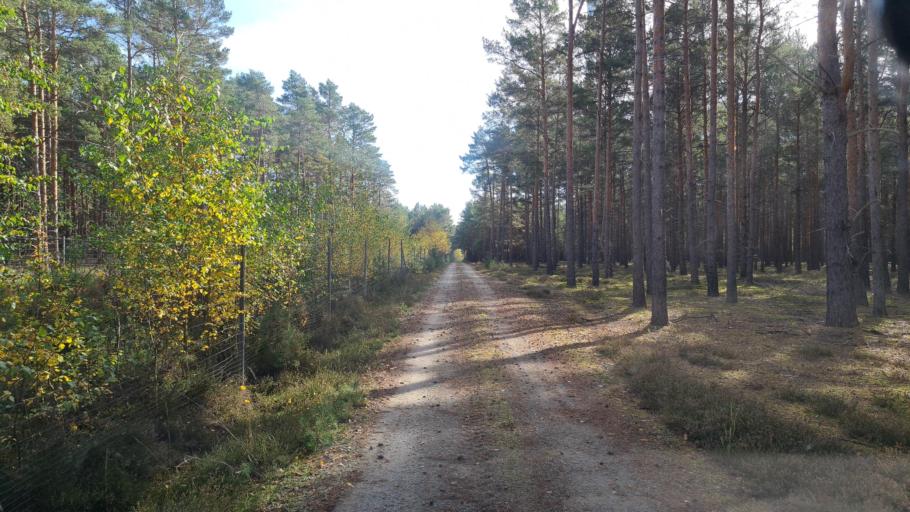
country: DE
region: Brandenburg
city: Sallgast
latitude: 51.6364
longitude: 13.8332
